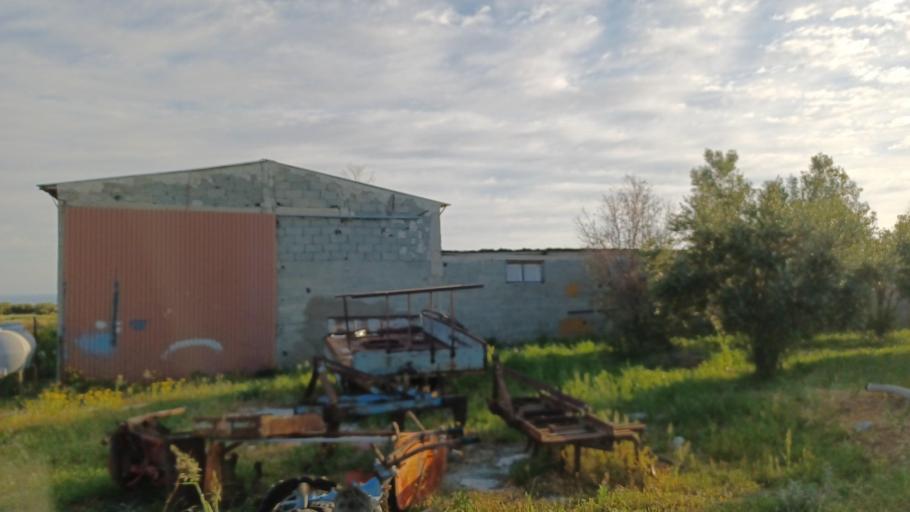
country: CY
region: Pafos
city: Polis
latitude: 35.0228
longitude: 32.4008
